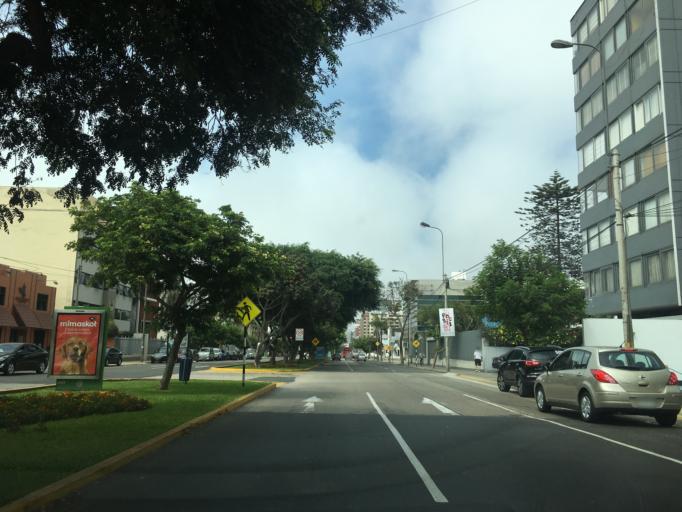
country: PE
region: Lima
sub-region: Lima
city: San Isidro
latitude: -12.1112
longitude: -77.0369
